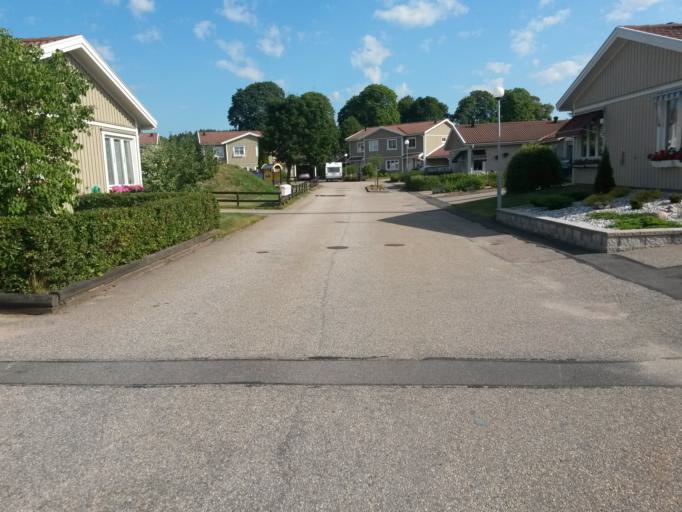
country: SE
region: Vaestra Goetaland
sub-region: Vargarda Kommun
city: Vargarda
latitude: 58.0417
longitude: 12.8129
